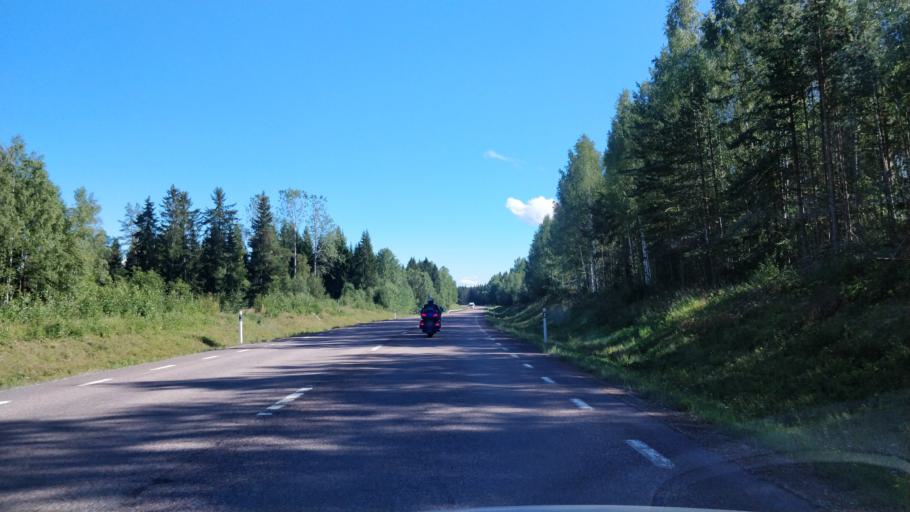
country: SE
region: Dalarna
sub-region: Faluns Kommun
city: Grycksbo
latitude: 60.6583
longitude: 15.5525
